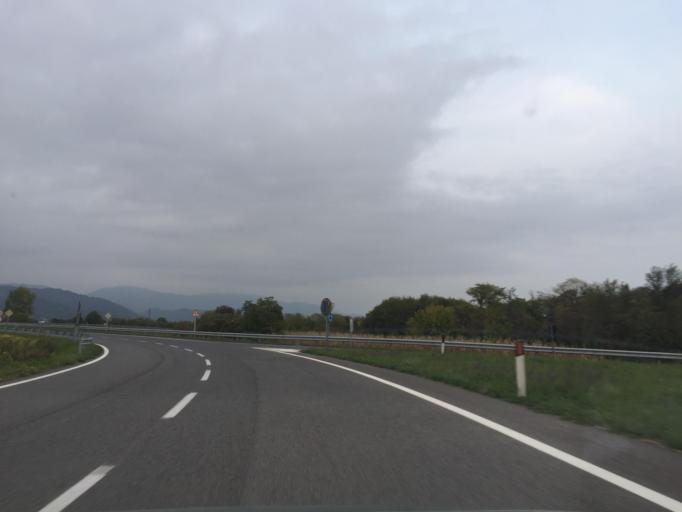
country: IT
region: Friuli Venezia Giulia
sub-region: Provincia di Pordenone
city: Vajont
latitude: 46.1535
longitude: 12.6917
